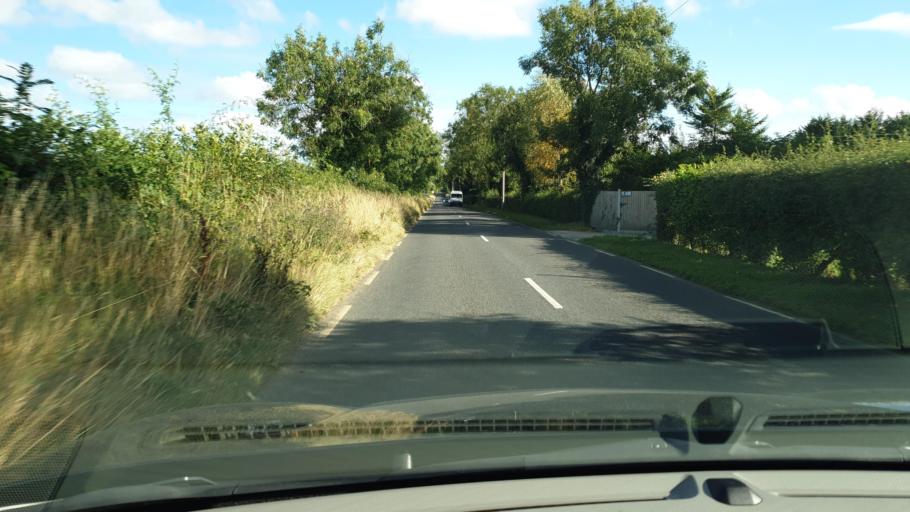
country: IE
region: Leinster
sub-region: An Mhi
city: Ashbourne
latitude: 53.4789
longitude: -6.4285
